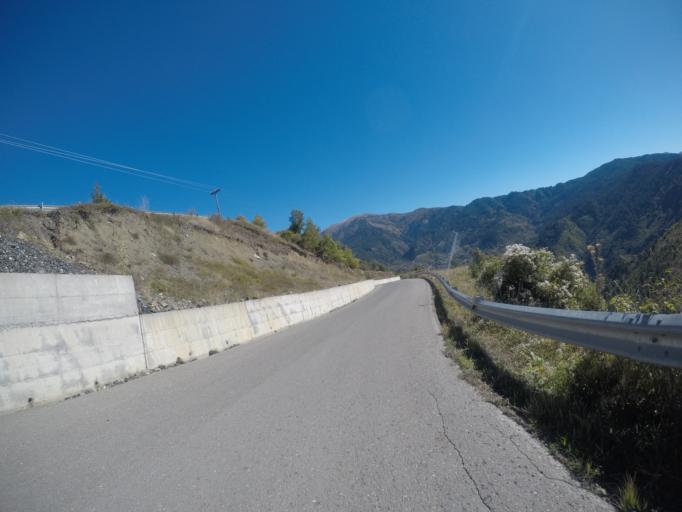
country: GR
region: Epirus
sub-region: Nomos Ioanninon
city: Konitsa
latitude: 40.0305
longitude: 20.9905
